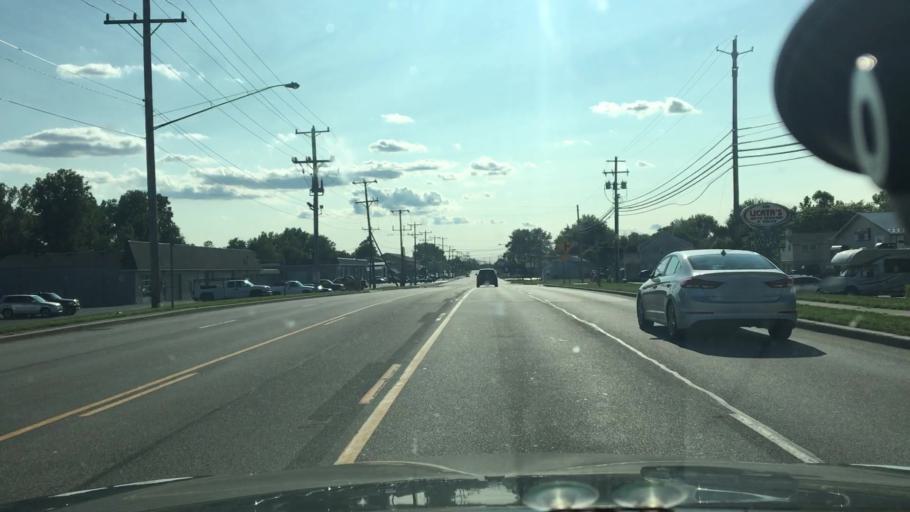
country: US
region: New York
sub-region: Erie County
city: Depew
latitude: 42.9105
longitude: -78.7059
